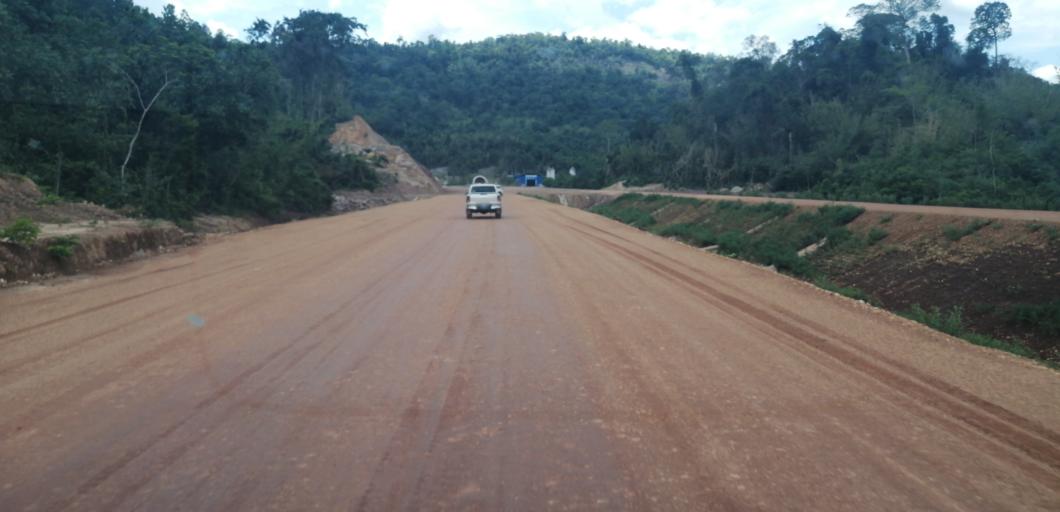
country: LA
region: Vientiane
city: Muang Phon-Hong
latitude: 18.5445
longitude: 102.3655
